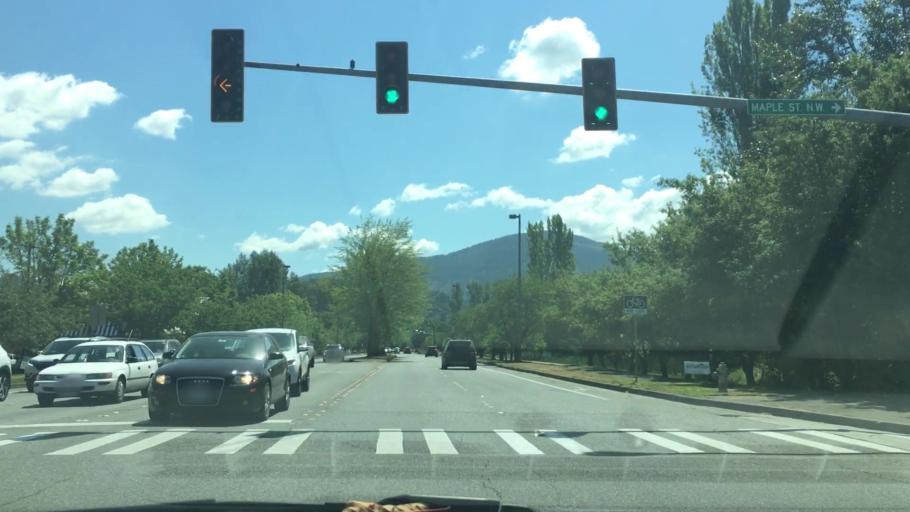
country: US
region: Washington
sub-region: King County
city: Issaquah
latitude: 47.5443
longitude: -122.0499
